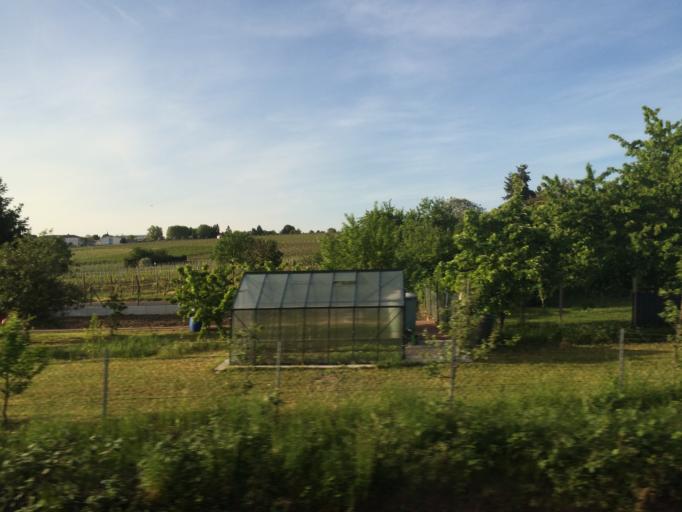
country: DE
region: Hesse
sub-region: Regierungsbezirk Darmstadt
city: Hochheim am Main
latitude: 50.0039
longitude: 8.3557
